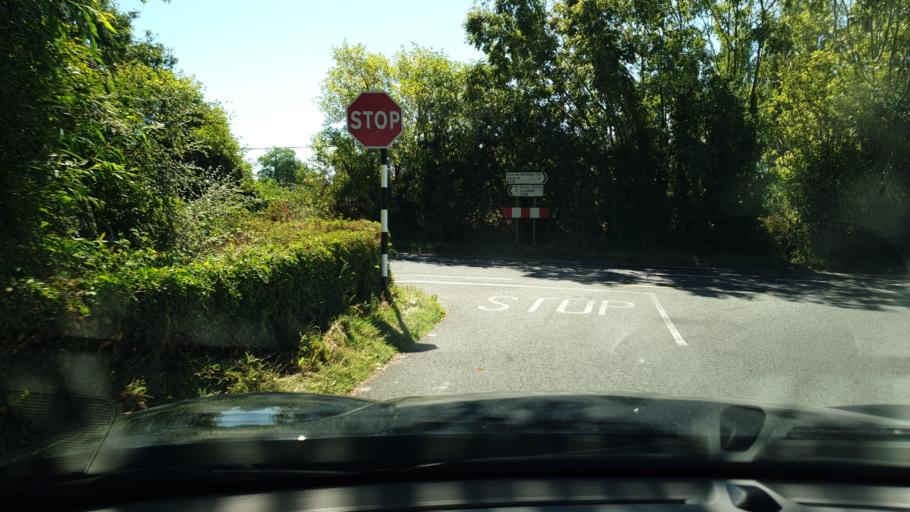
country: IE
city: Confey
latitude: 53.3754
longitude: -6.4803
